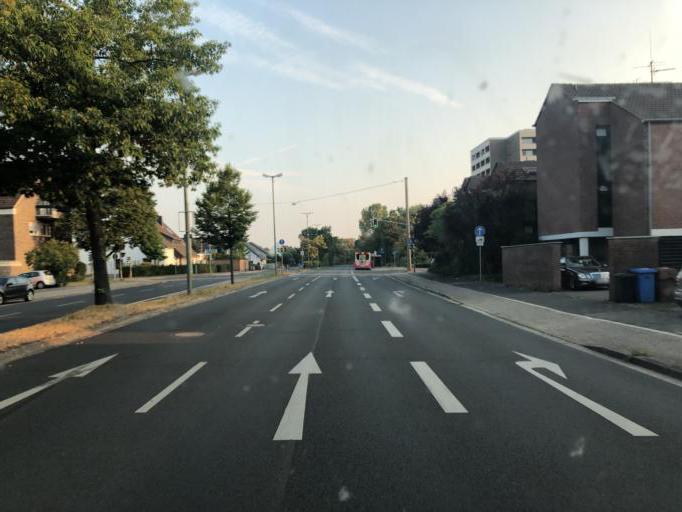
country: DE
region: North Rhine-Westphalia
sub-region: Regierungsbezirk Dusseldorf
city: Neuss
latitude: 51.1884
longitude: 6.6706
